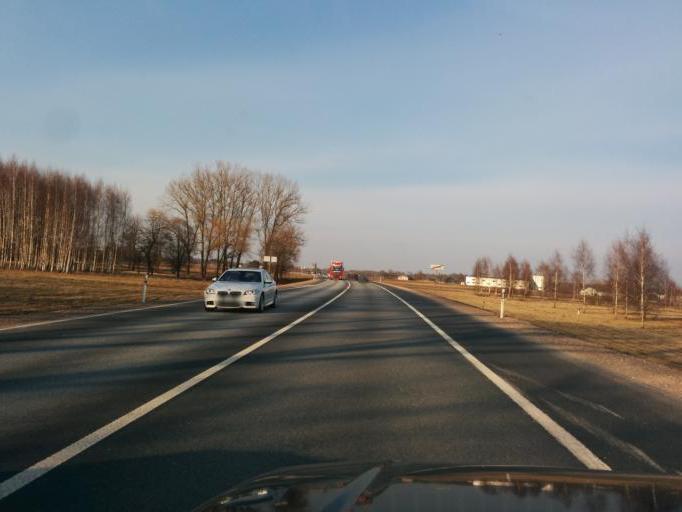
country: LV
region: Lecava
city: Iecava
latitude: 56.6075
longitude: 24.2111
